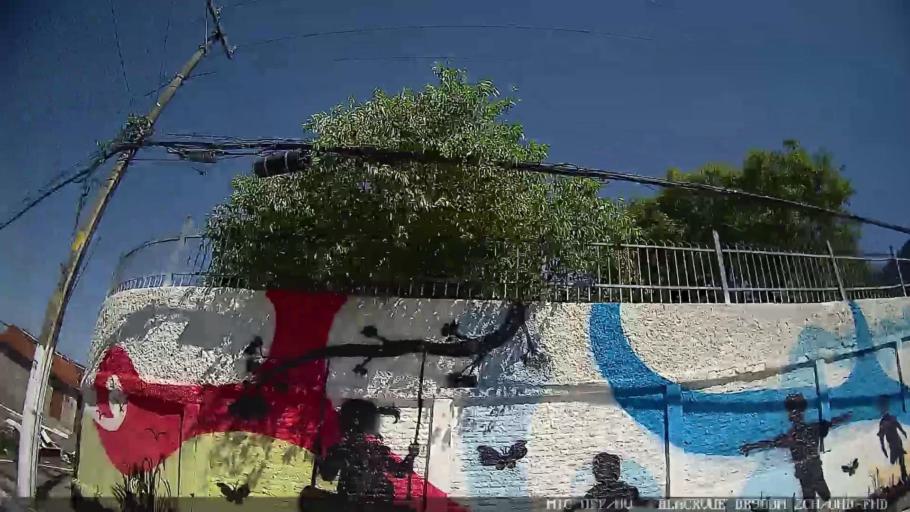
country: BR
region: Sao Paulo
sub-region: Sao Caetano Do Sul
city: Sao Caetano do Sul
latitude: -23.5890
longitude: -46.4979
